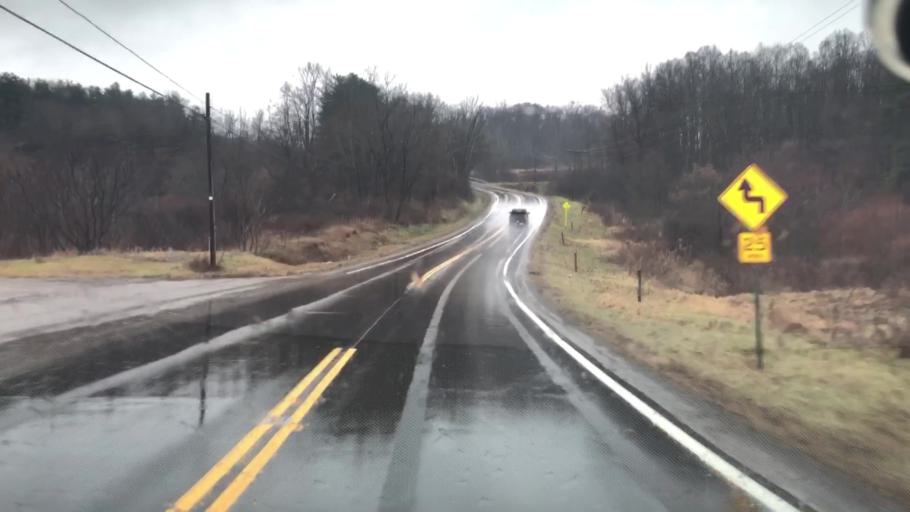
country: US
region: Ohio
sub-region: Harrison County
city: Cadiz
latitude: 40.2048
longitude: -80.9951
